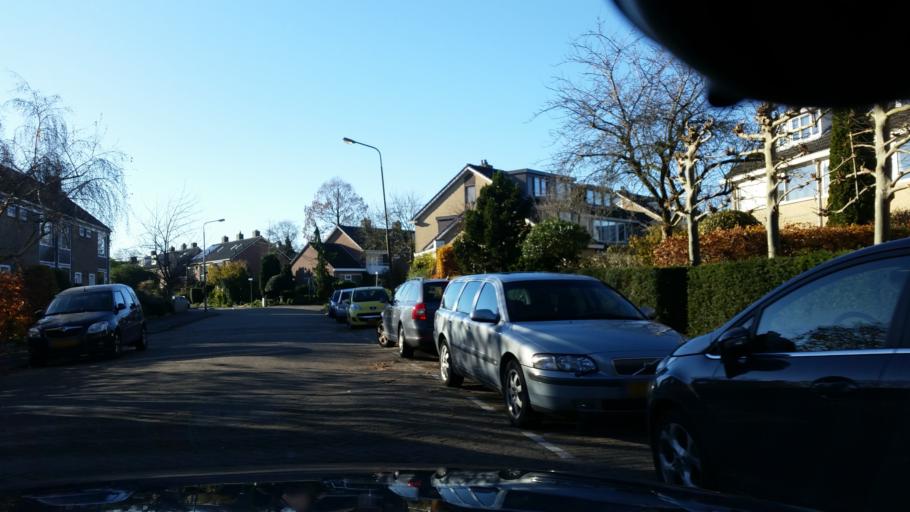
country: NL
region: North Holland
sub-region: Gemeente Ouder-Amstel
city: Ouderkerk aan de Amstel
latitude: 52.2970
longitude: 4.9131
